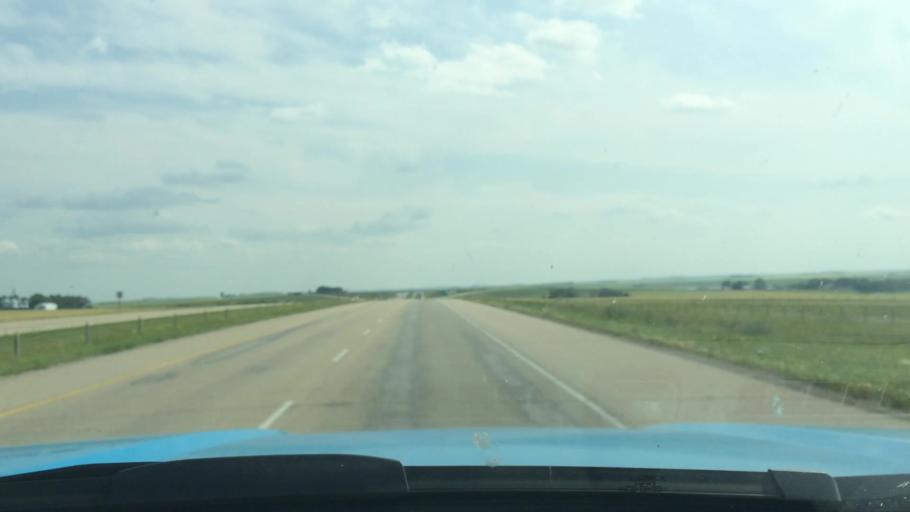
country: CA
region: Alberta
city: Carstairs
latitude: 51.5727
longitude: -114.0254
